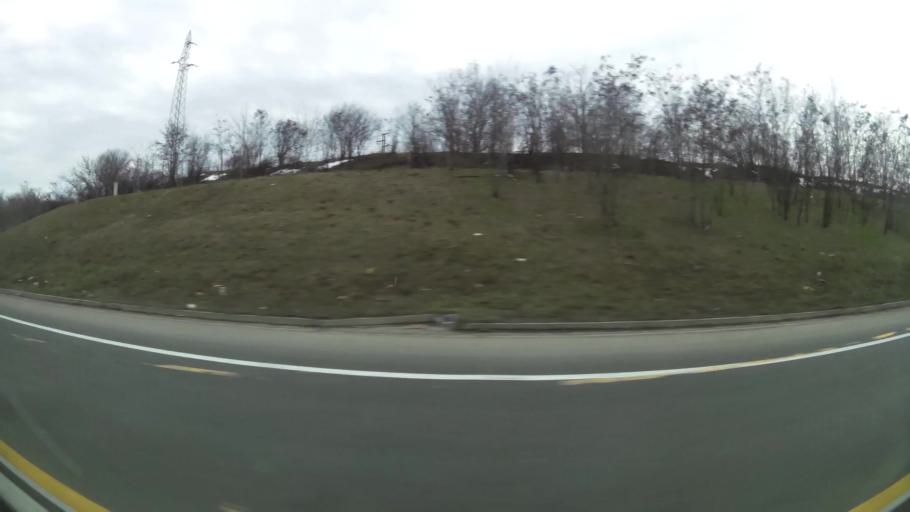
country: RS
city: Ostruznica
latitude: 44.7219
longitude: 20.3587
